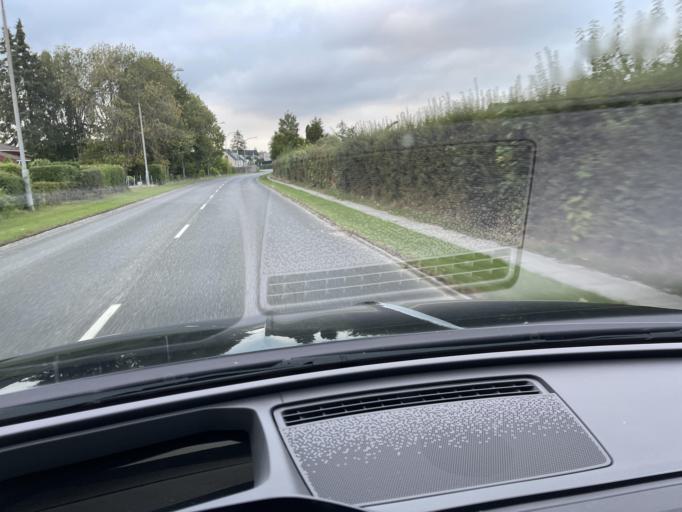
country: DK
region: Zealand
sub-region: Solrod Kommune
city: Havdrup
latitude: 55.5442
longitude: 12.1213
